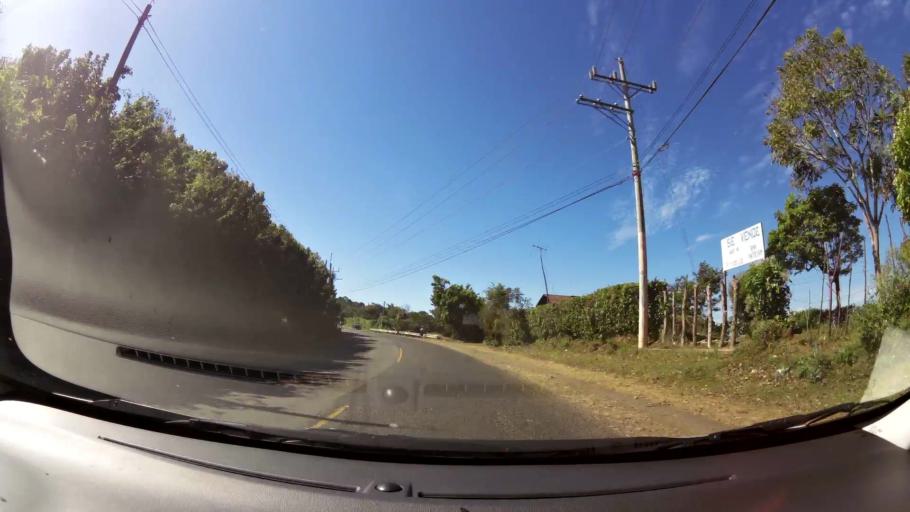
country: SV
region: Ahuachapan
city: Concepcion de Ataco
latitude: 13.8619
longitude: -89.8051
